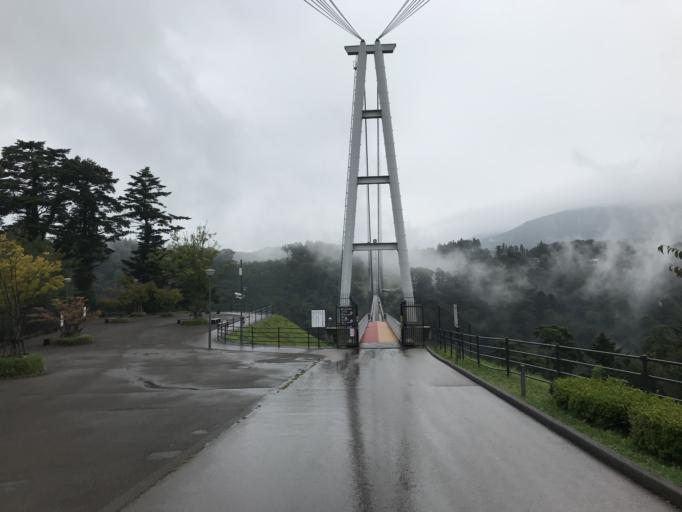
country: JP
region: Oita
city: Tsukawaki
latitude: 33.1721
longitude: 131.2248
